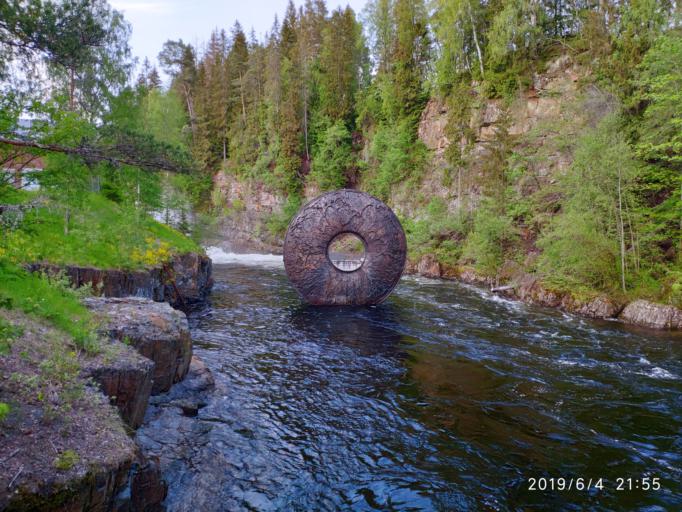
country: NO
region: Oppland
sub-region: Jevnaker
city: Jevnaker
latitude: 60.2210
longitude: 10.3689
